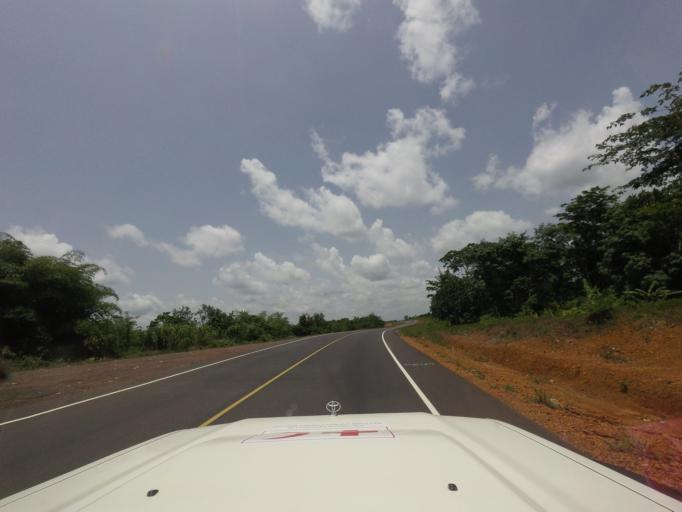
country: LR
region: Margibi
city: Kakata
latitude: 6.4672
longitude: -10.4157
